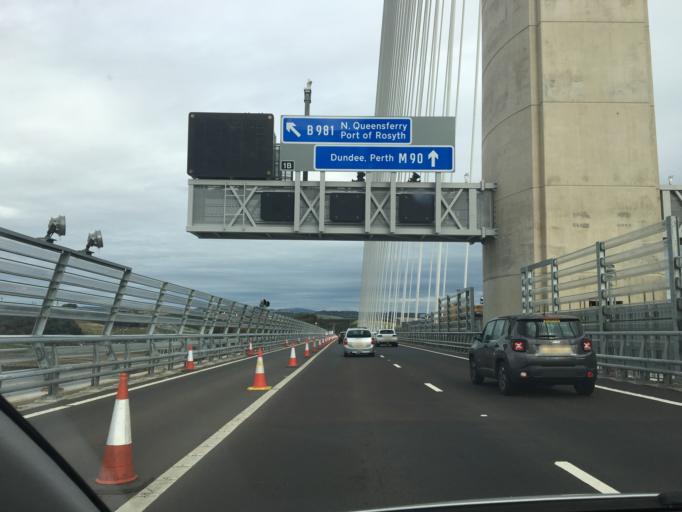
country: GB
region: Scotland
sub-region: Fife
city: North Queensferry
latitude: 56.0101
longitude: -3.4093
